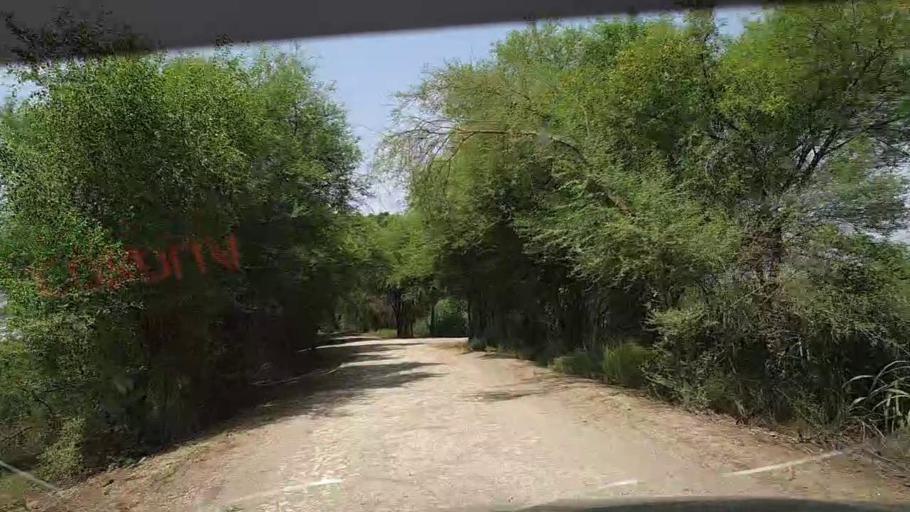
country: PK
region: Sindh
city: Ghotki
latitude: 28.0945
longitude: 69.3129
